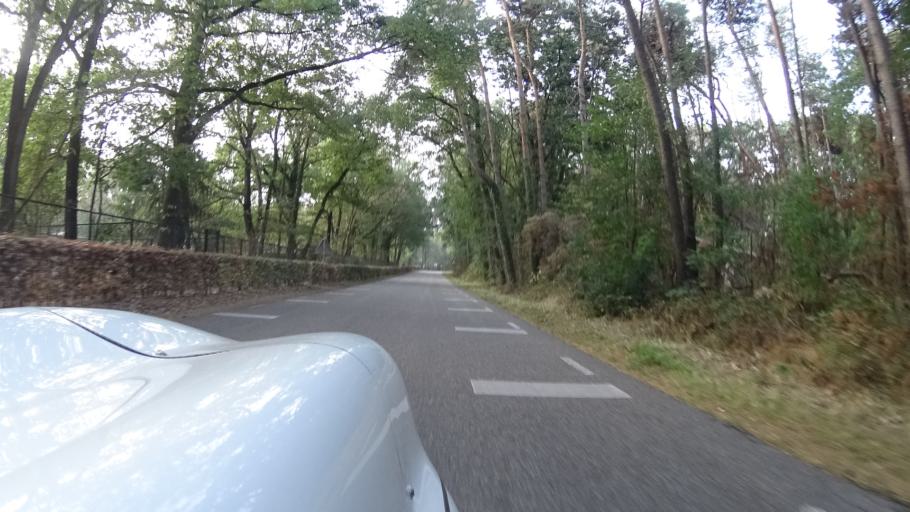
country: NL
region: Limburg
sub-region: Gemeente Venlo
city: Arcen
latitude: 51.4901
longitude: 6.2071
